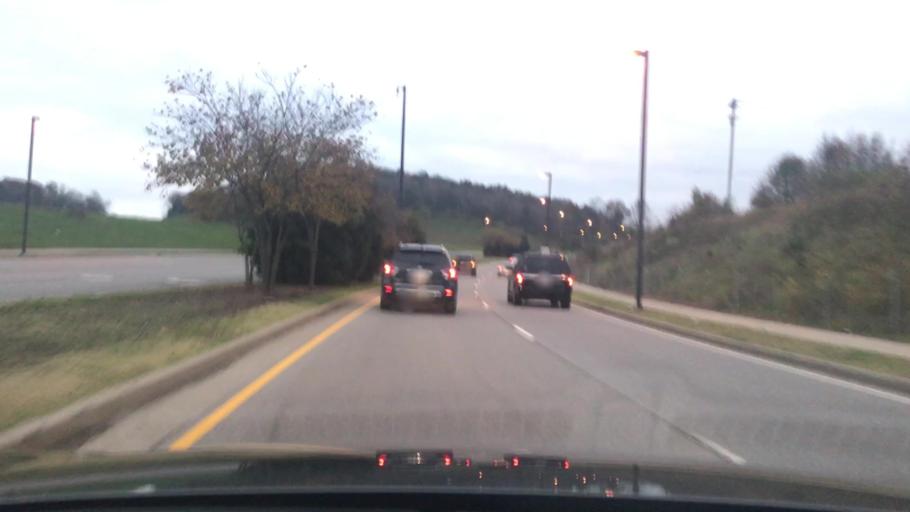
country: US
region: Tennessee
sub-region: Williamson County
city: Franklin
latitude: 35.9326
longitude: -86.8119
